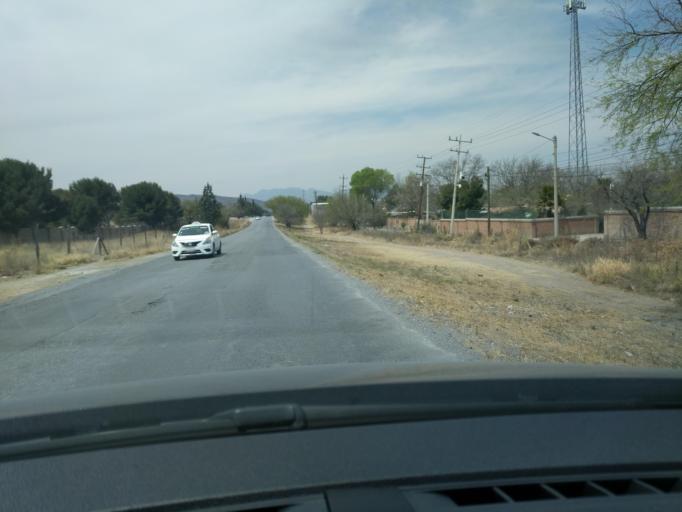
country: MX
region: Coahuila
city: Saltillo
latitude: 25.3537
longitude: -101.0265
